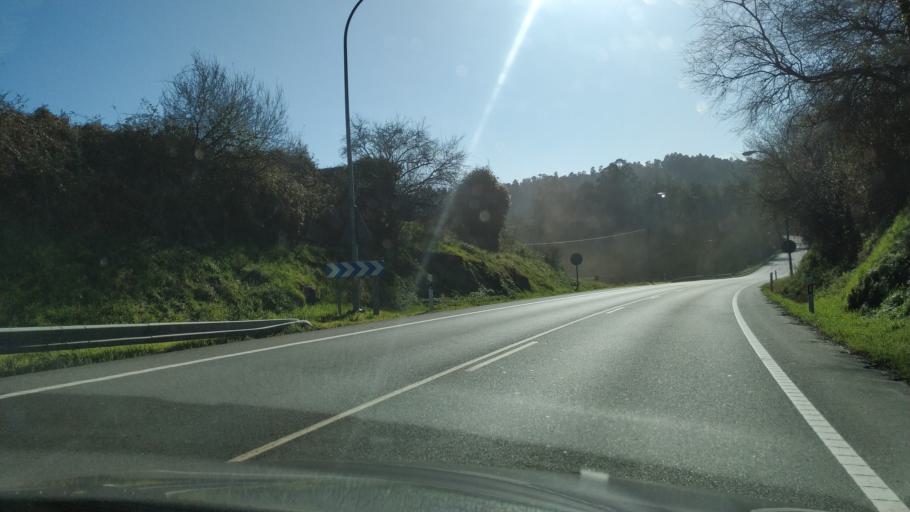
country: ES
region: Galicia
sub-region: Provincia de Pontevedra
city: Silleda
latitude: 42.7339
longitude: -8.3205
